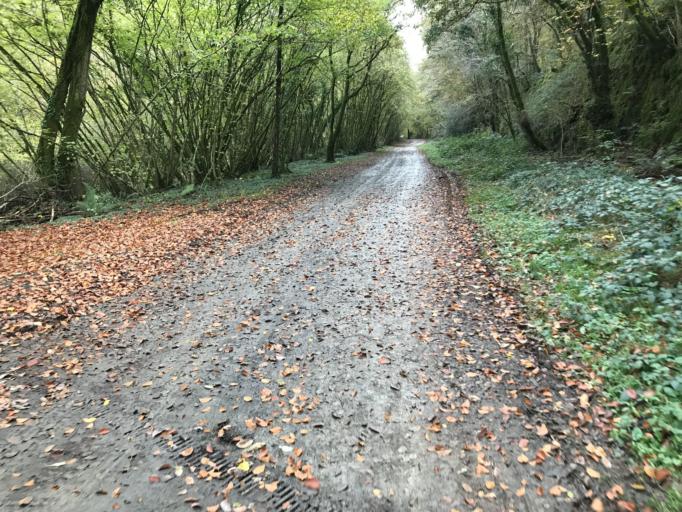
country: FR
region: Brittany
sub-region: Departement du Finistere
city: Irvillac
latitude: 48.3424
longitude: -4.2106
